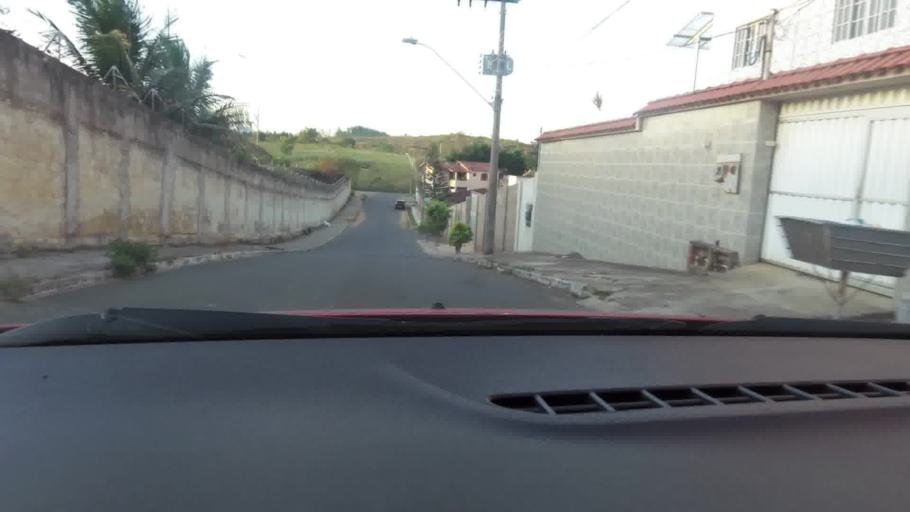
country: BR
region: Espirito Santo
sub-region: Guarapari
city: Guarapari
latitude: -20.6511
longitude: -40.5043
